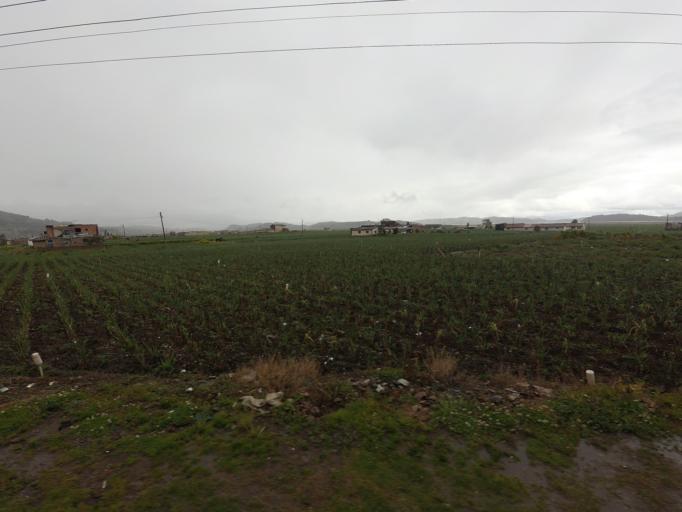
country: CO
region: Boyaca
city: Aquitania
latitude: 5.5273
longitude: -72.8838
